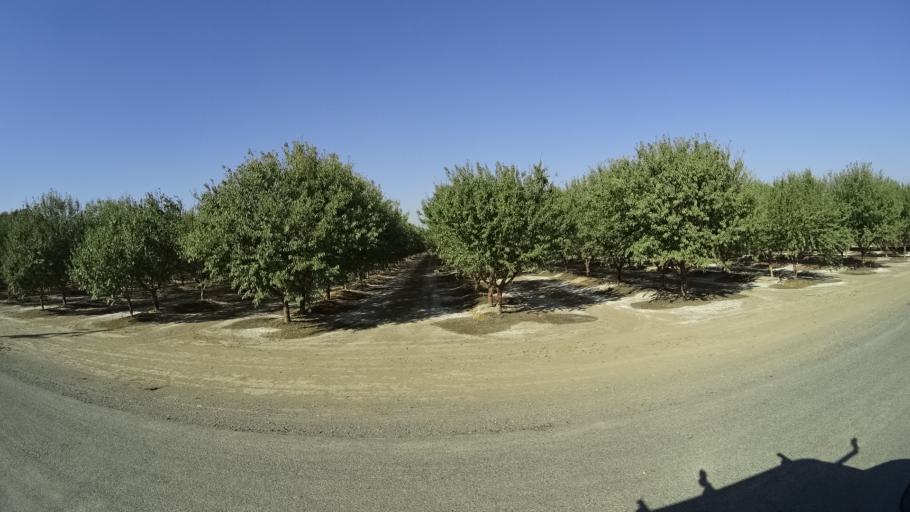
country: US
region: California
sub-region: Yolo County
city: Woodland
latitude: 38.7495
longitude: -121.7787
